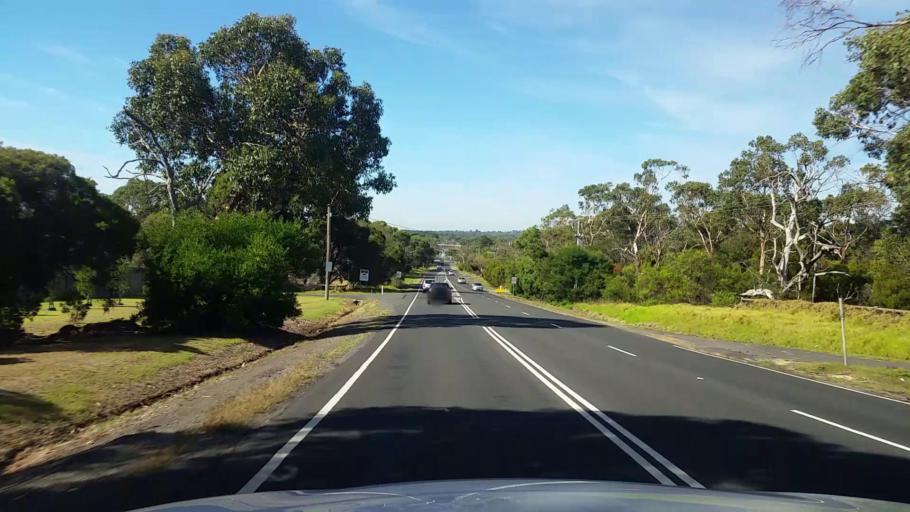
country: AU
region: Victoria
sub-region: Mornington Peninsula
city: Baxter
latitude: -38.1897
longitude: 145.1455
